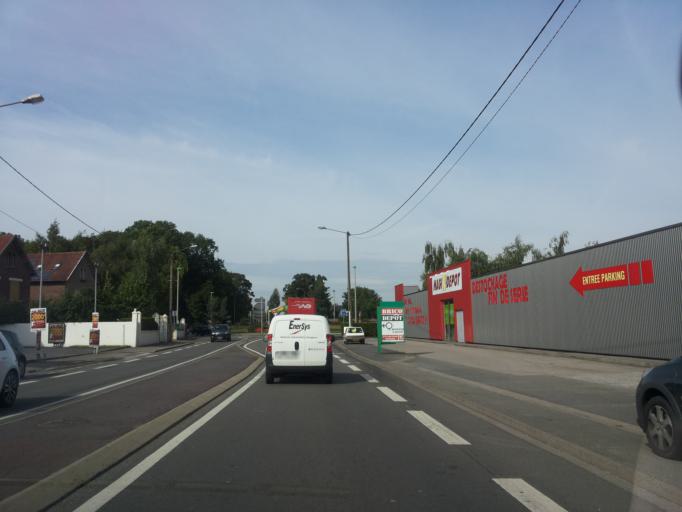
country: FR
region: Nord-Pas-de-Calais
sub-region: Departement du Pas-de-Calais
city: Tilloy-les-Mofflaines
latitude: 50.2797
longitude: 2.8159
